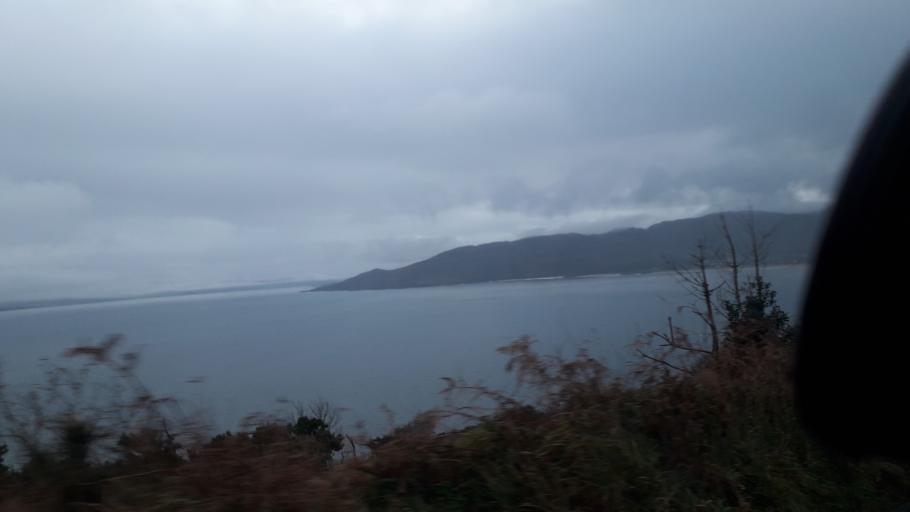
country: IE
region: Ulster
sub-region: County Donegal
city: Ramelton
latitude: 55.2134
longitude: -7.6143
